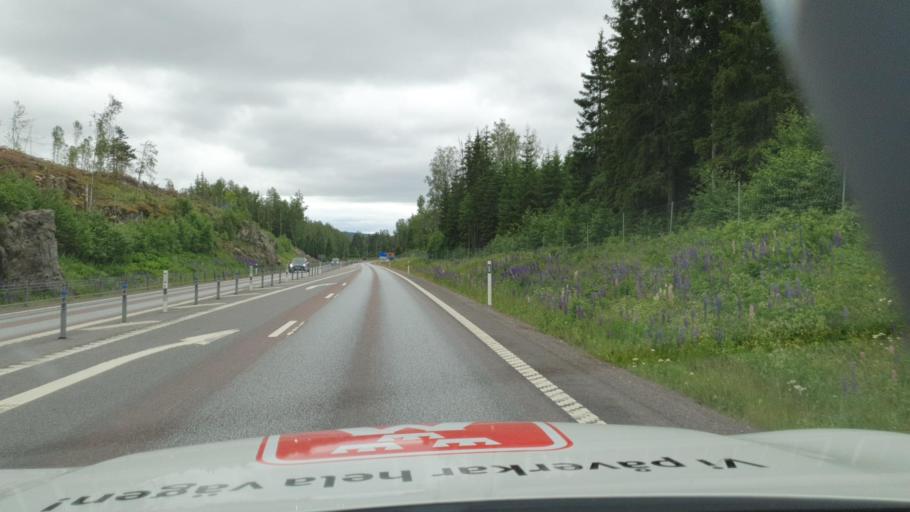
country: SE
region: Vaermland
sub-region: Arvika Kommun
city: Arvika
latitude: 59.6521
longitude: 12.7547
